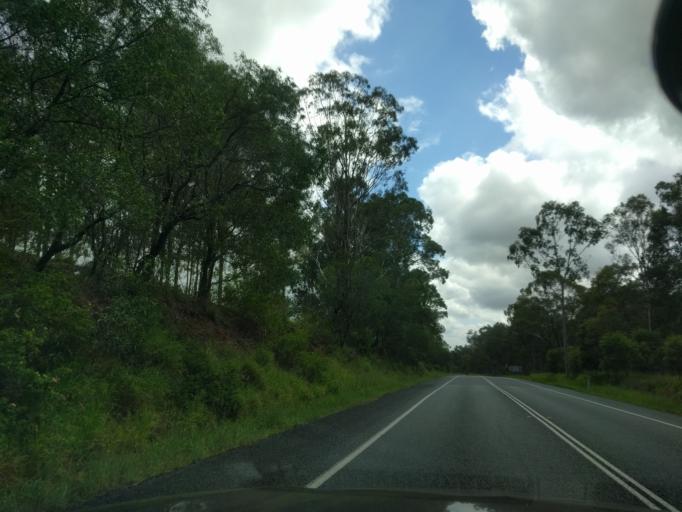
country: AU
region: Queensland
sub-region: Logan
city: Cedar Vale
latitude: -27.8737
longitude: 152.9943
